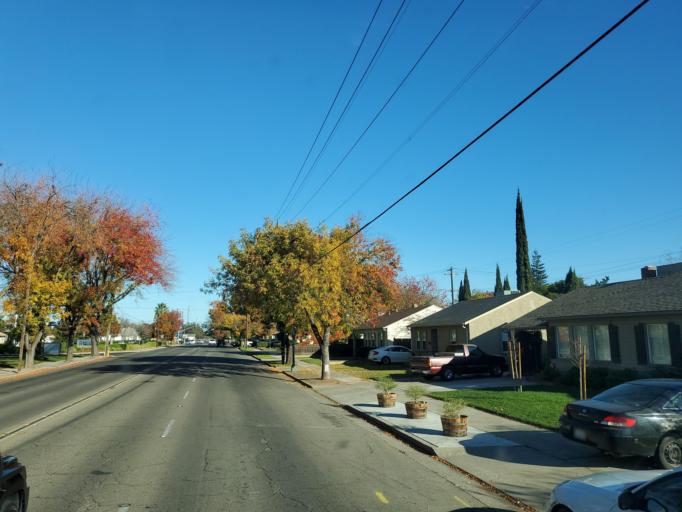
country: US
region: California
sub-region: San Joaquin County
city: Stockton
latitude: 37.9794
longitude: -121.3019
